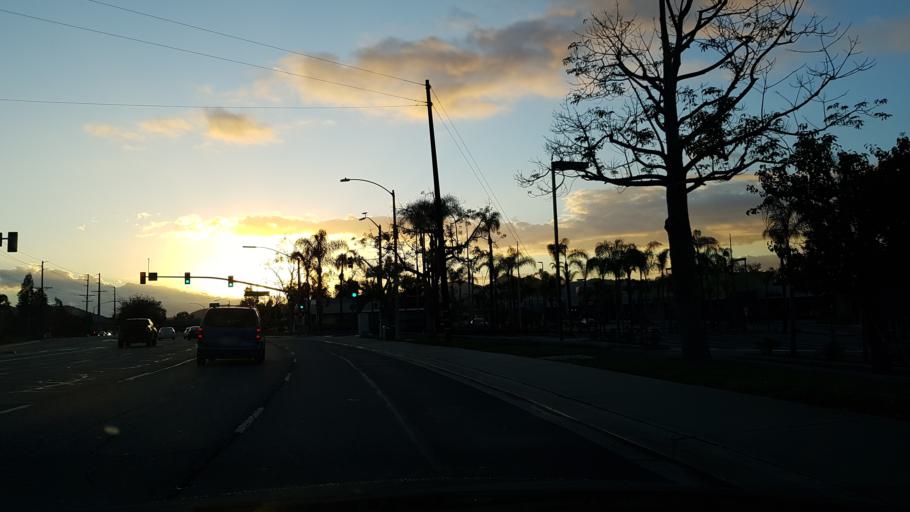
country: US
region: California
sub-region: San Diego County
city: Escondido
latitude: 33.1175
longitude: -117.0956
